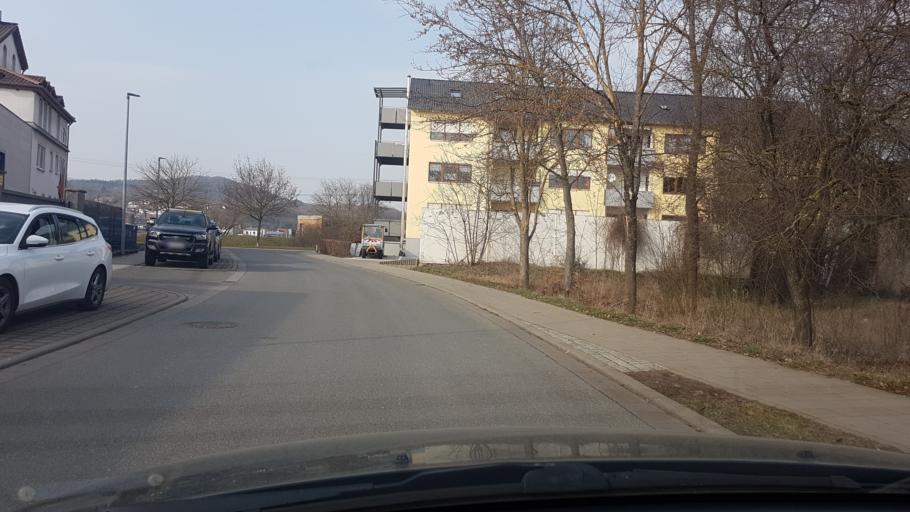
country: DE
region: Bavaria
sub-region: Upper Franconia
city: Hallstadt
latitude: 49.9259
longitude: 10.8669
